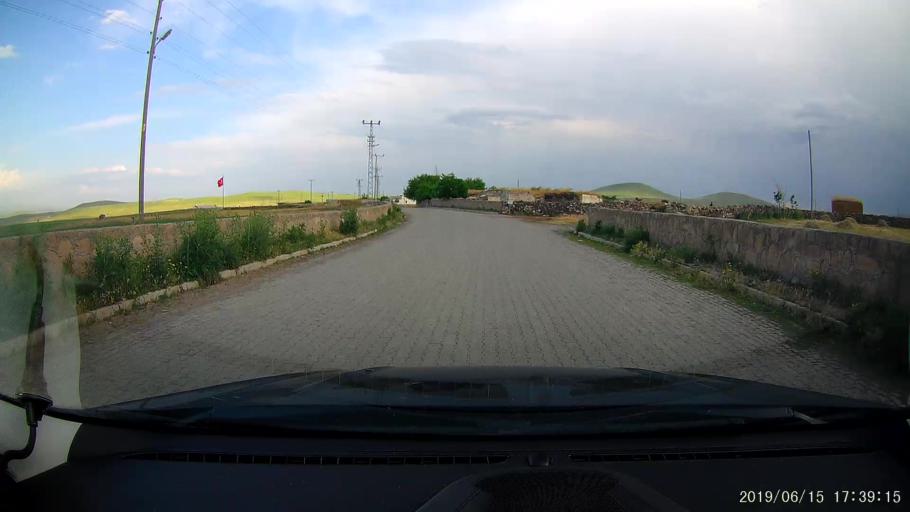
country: TR
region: Kars
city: Basgedikler
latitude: 40.5170
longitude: 43.5696
